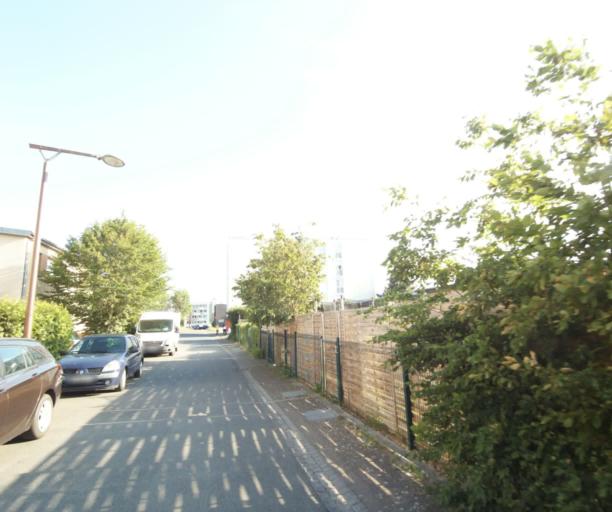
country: FR
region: Champagne-Ardenne
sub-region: Departement des Ardennes
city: Charleville-Mezieres
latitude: 49.7852
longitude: 4.7101
